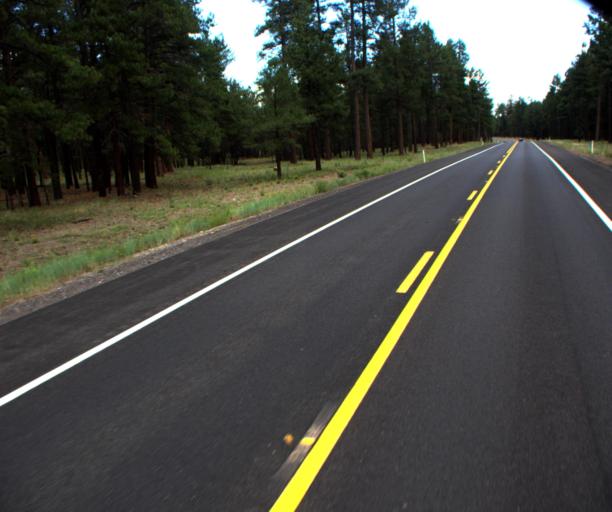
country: US
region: Arizona
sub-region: Coconino County
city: Flagstaff
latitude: 35.2541
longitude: -111.7005
